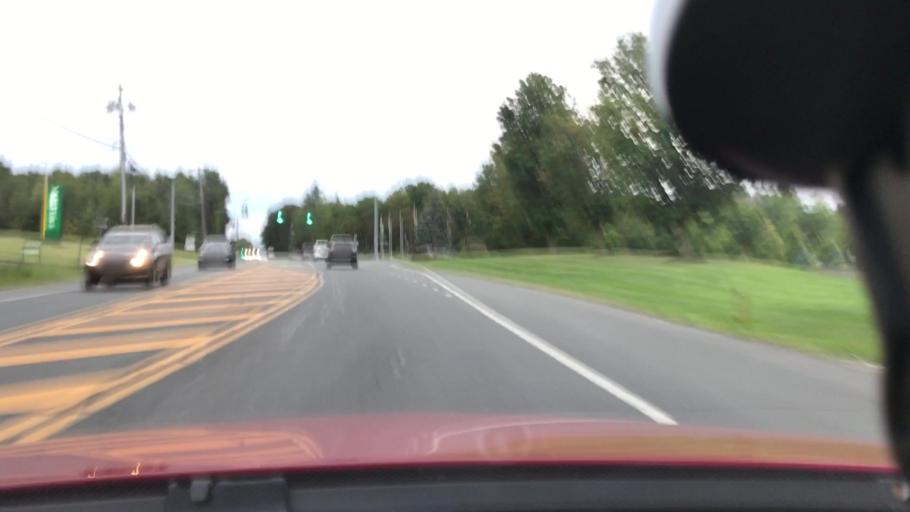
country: US
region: New York
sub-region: Albany County
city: Menands
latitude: 42.6776
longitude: -73.6906
